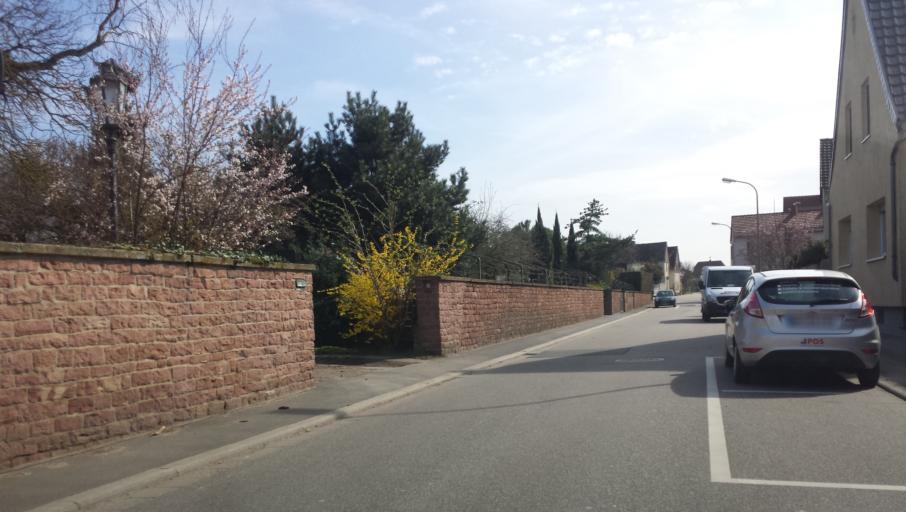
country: DE
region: Rheinland-Pfalz
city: Dudenhofen
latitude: 49.2894
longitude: 8.4080
